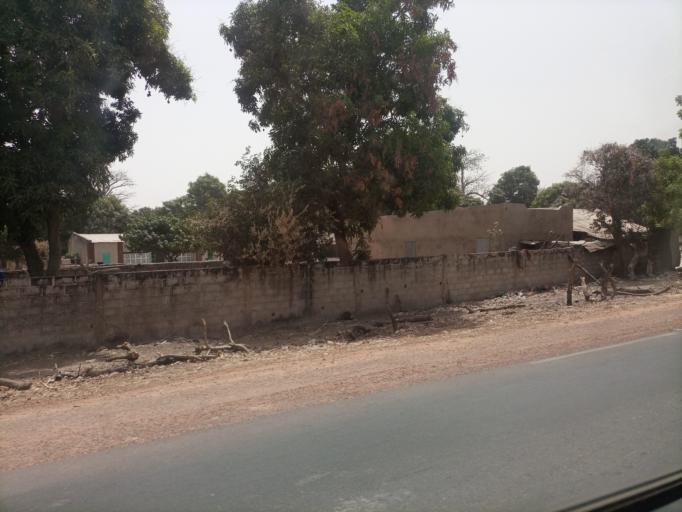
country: SN
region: Fatick
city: Sokone
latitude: 13.7060
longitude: -16.4290
